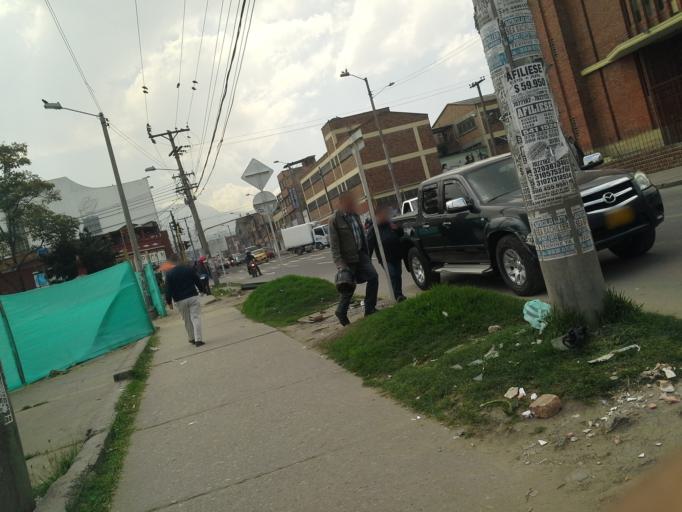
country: CO
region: Bogota D.C.
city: Bogota
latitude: 4.5825
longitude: -74.1087
